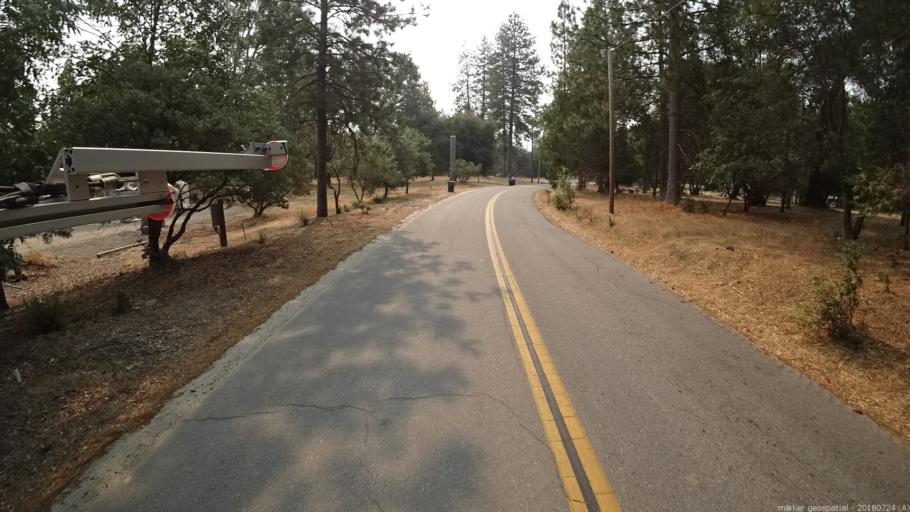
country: US
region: California
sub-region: Madera County
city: Oakhurst
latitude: 37.3051
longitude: -119.6150
